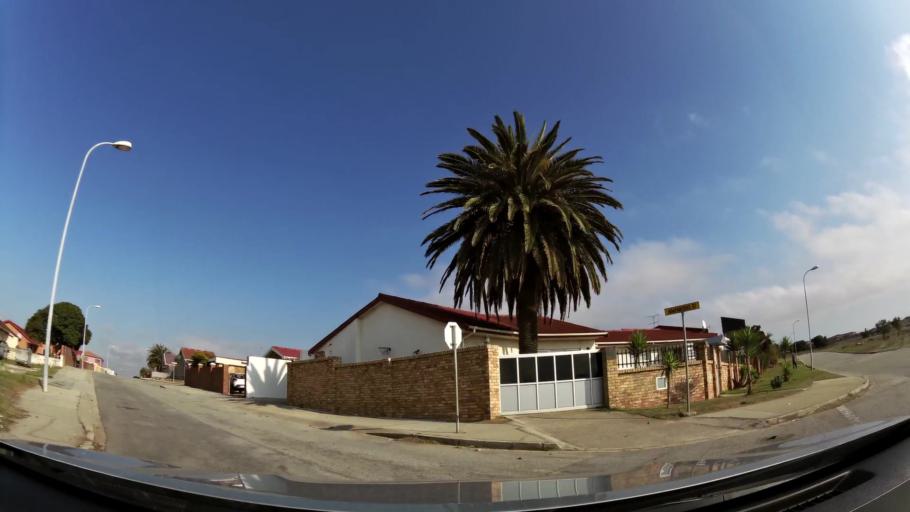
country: ZA
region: Eastern Cape
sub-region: Nelson Mandela Bay Metropolitan Municipality
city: Port Elizabeth
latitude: -33.9225
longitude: 25.5398
